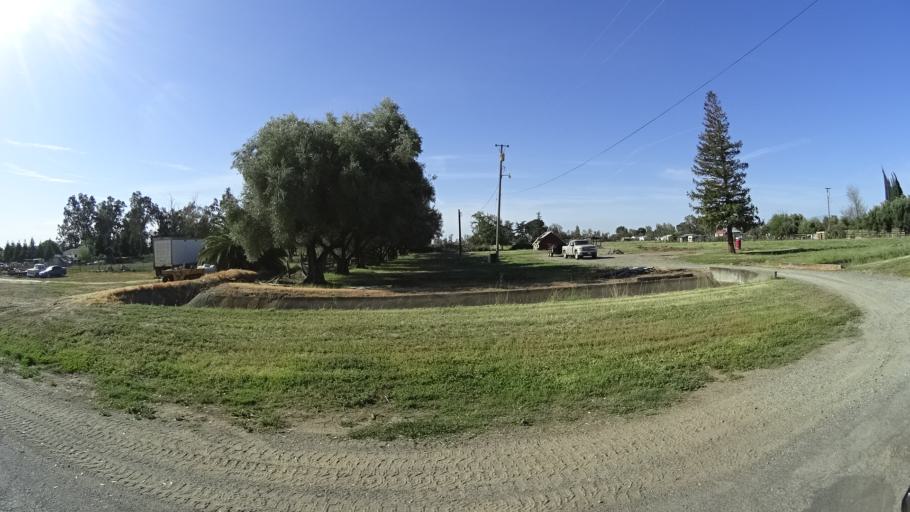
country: US
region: California
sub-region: Glenn County
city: Orland
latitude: 39.7150
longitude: -122.1994
